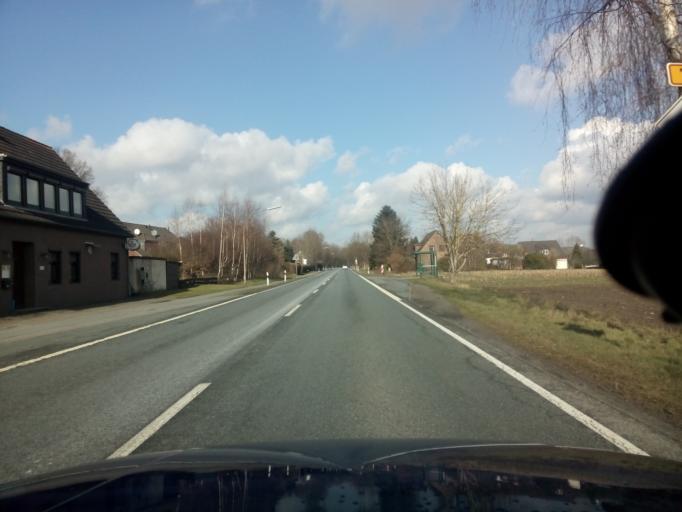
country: DE
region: Lower Saxony
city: Osterholz-Scharmbeck
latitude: 53.2646
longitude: 8.8170
